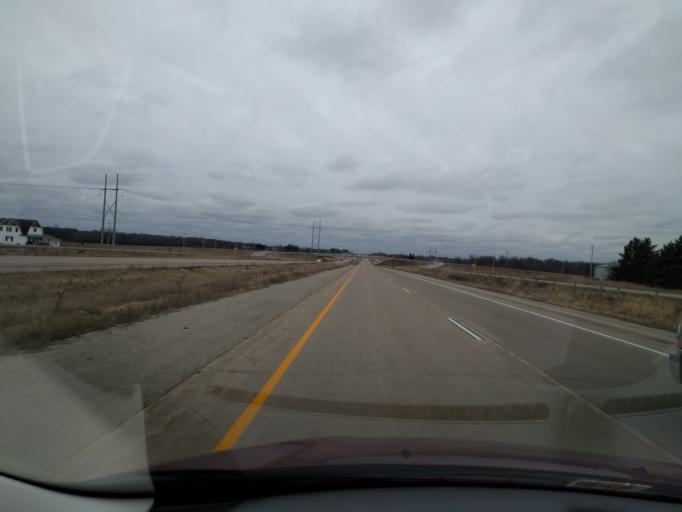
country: US
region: Wisconsin
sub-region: Winnebago County
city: Winneconne
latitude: 44.1740
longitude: -88.6645
